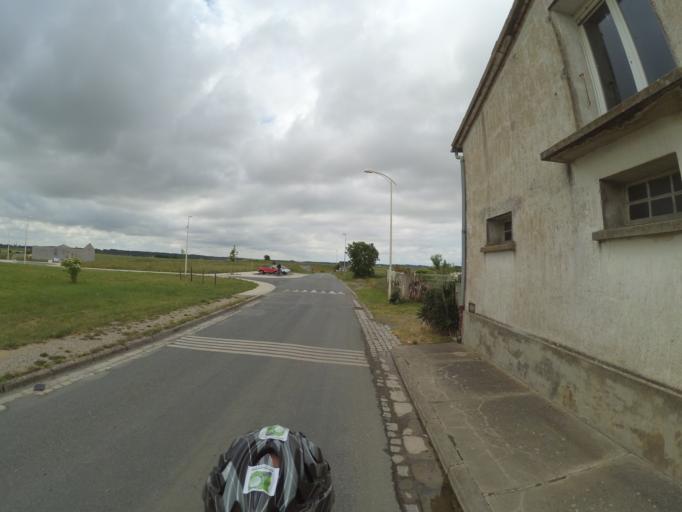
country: FR
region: Poitou-Charentes
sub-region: Departement de la Charente-Maritime
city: Yves
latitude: 46.0173
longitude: -1.0487
